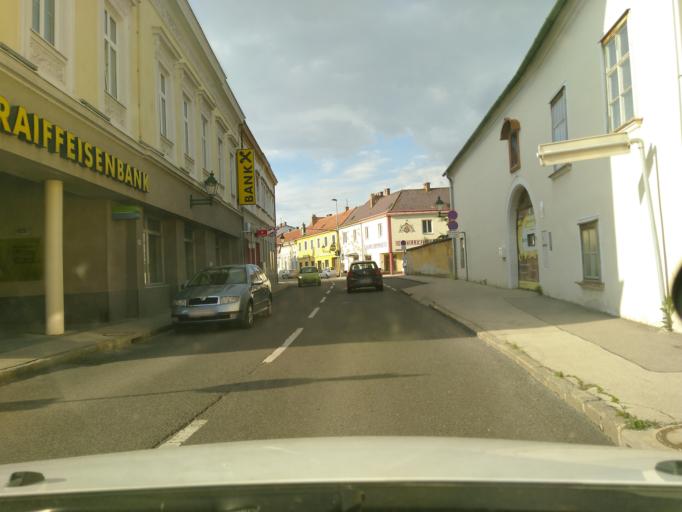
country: AT
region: Lower Austria
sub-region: Politischer Bezirk Modling
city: Maria Enzersdorf
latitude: 48.0985
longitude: 16.2840
